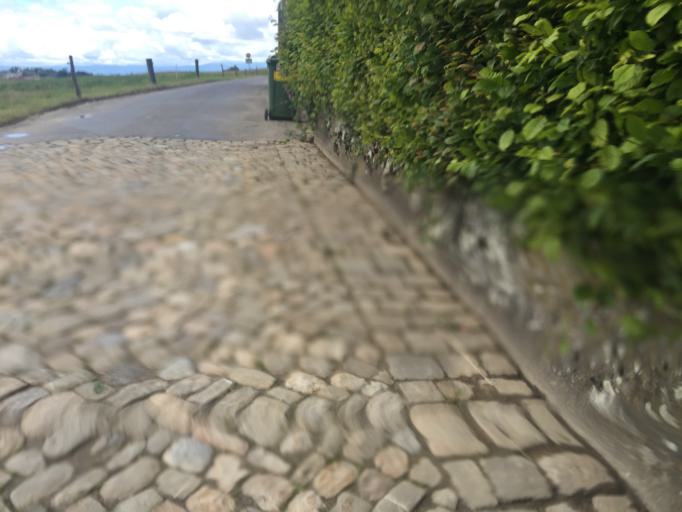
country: CH
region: Bern
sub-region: Bern-Mittelland District
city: Wohlen
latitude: 46.9502
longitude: 7.3601
